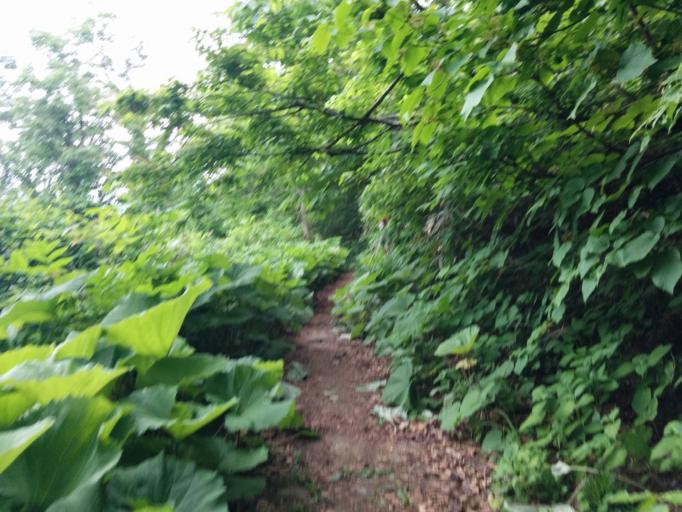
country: JP
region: Aomori
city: Hirosaki
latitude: 40.5562
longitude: 140.1636
